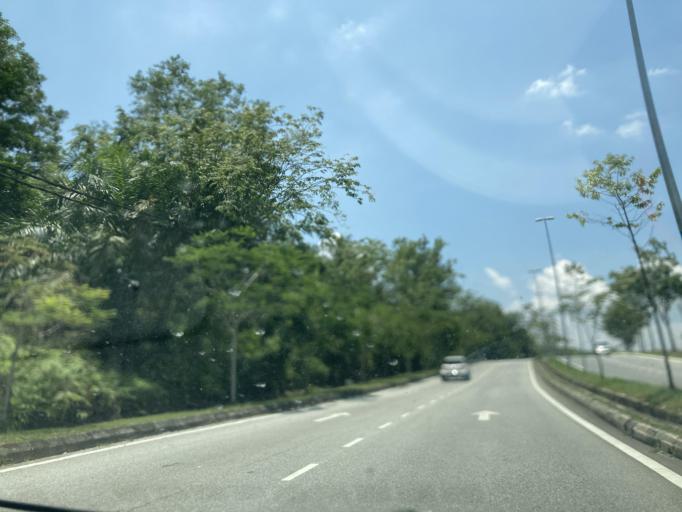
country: MY
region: Selangor
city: Batu Arang
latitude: 3.2922
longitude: 101.4808
